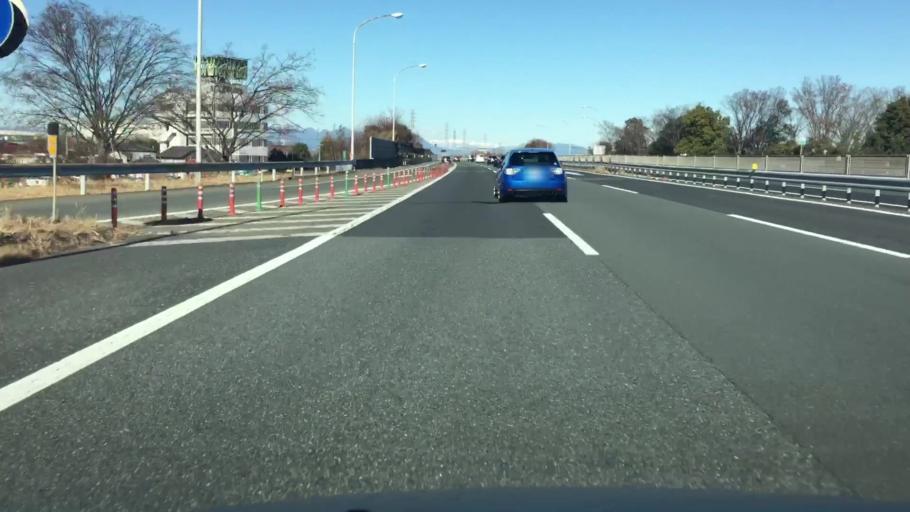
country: JP
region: Saitama
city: Honjo
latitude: 36.2184
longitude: 139.1645
